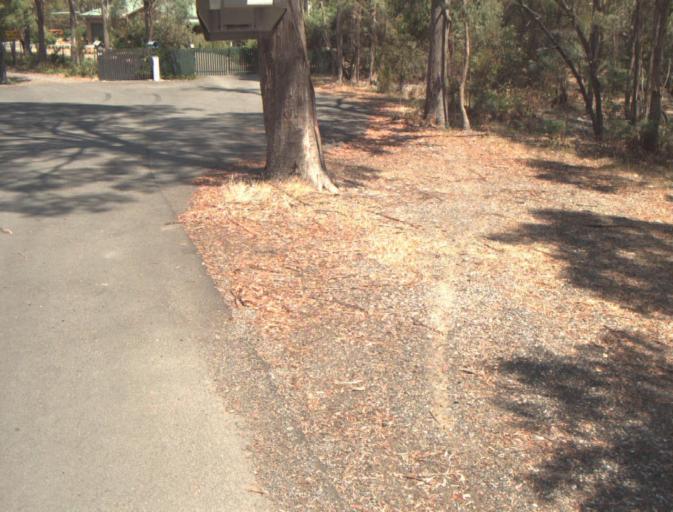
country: AU
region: Tasmania
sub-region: Launceston
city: Newstead
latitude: -41.4924
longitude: 147.1954
